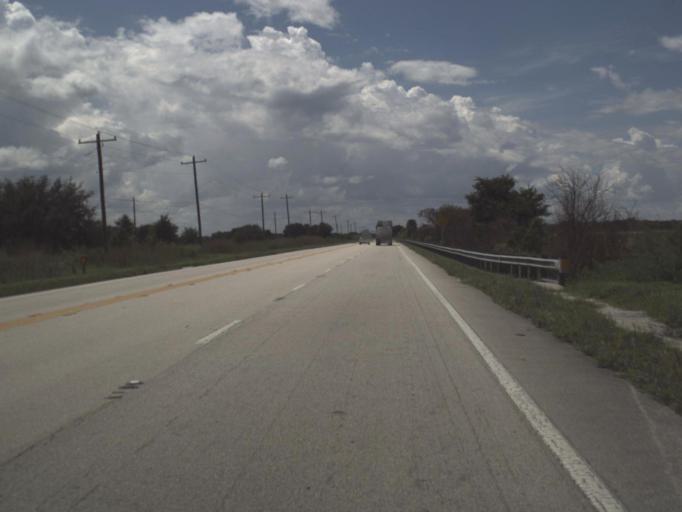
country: US
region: Florida
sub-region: Polk County
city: Babson Park
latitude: 27.8052
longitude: -81.2371
